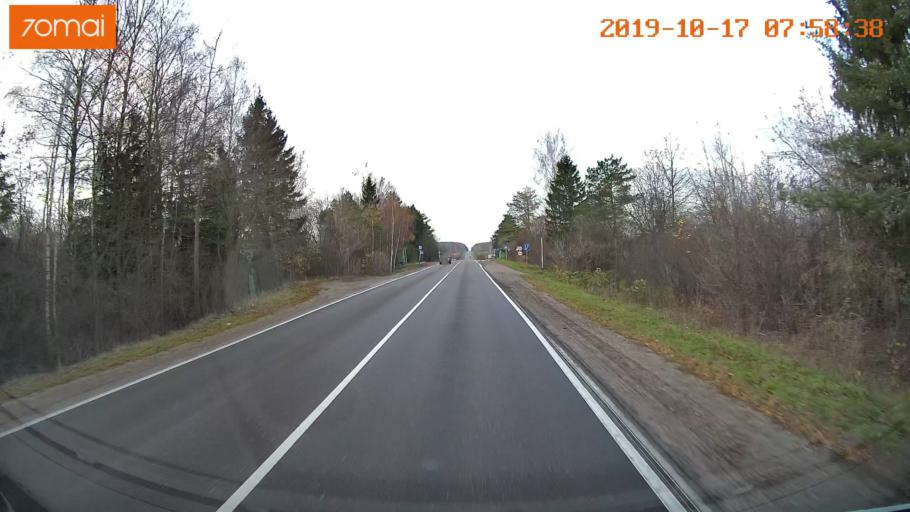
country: RU
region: Vladimir
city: Bavleny
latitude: 56.4008
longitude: 39.5537
